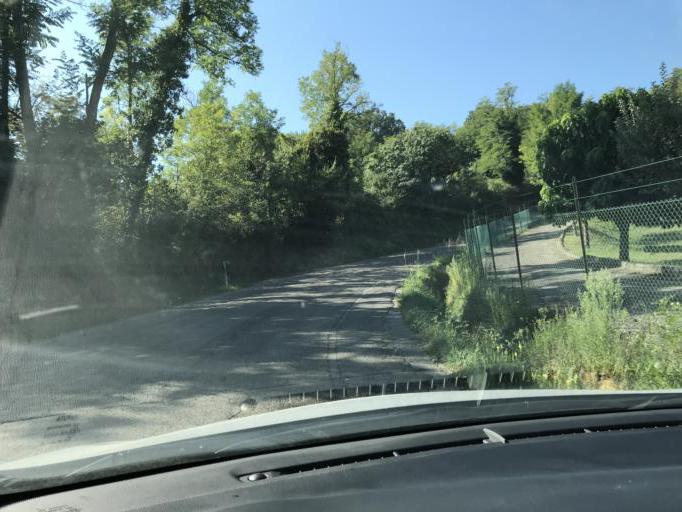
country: IT
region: Umbria
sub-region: Provincia di Perugia
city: Ponte Felcino
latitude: 43.1068
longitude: 12.4401
